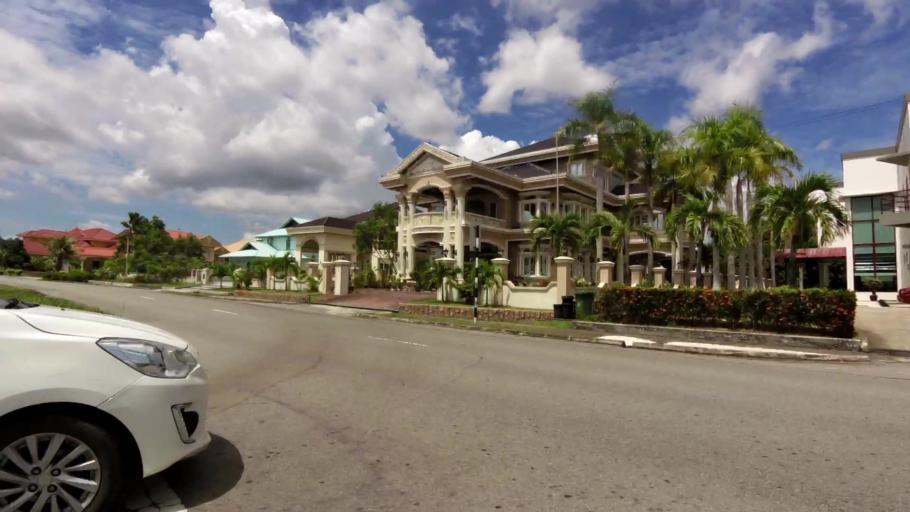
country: BN
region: Brunei and Muara
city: Bandar Seri Begawan
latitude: 4.9484
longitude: 114.9084
